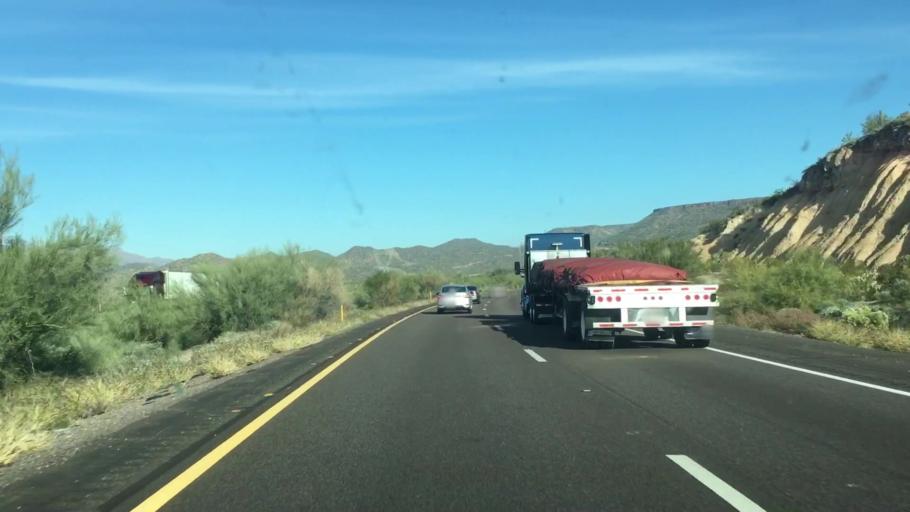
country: US
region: Arizona
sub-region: Yavapai County
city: Black Canyon City
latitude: 34.0821
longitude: -112.1360
